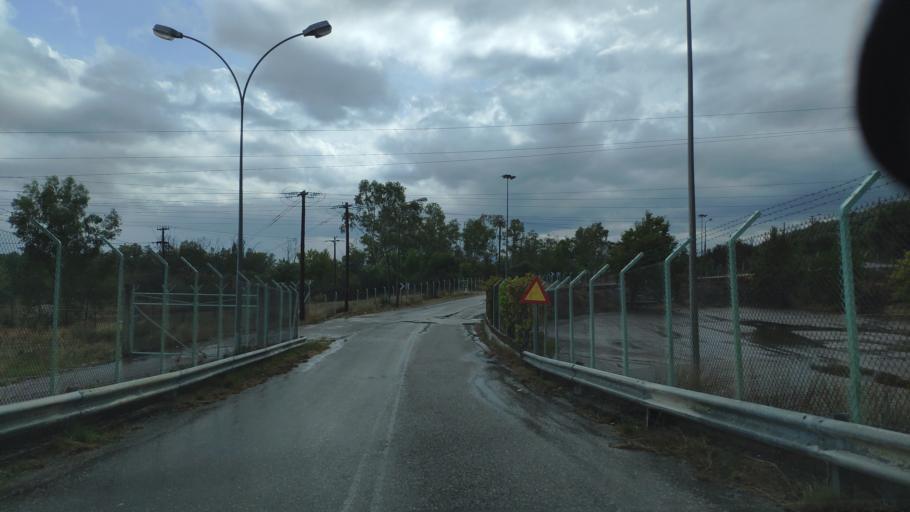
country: GR
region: West Greece
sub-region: Nomos Aitolias kai Akarnanias
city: Neapolis
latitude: 38.6755
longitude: 21.3250
